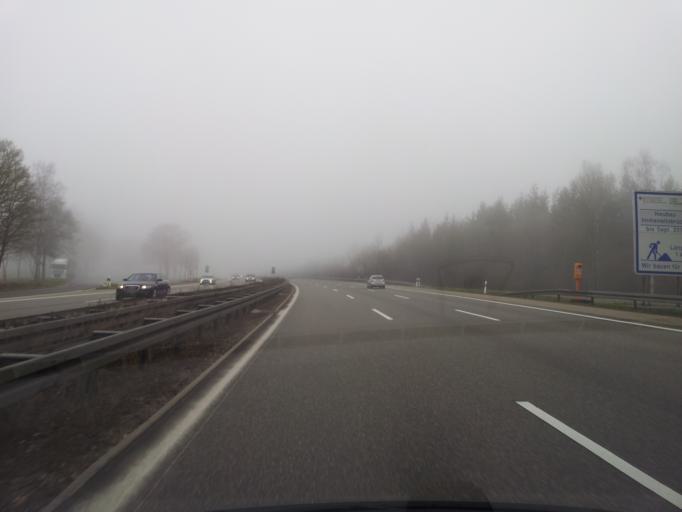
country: DE
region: Baden-Wuerttemberg
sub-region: Freiburg Region
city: Engen
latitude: 47.8900
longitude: 8.7701
